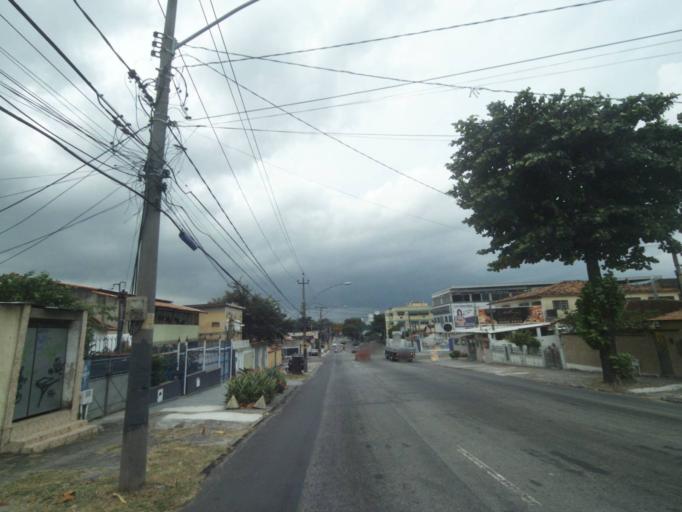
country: BR
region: Rio de Janeiro
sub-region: Nilopolis
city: Nilopolis
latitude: -22.8886
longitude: -43.3904
